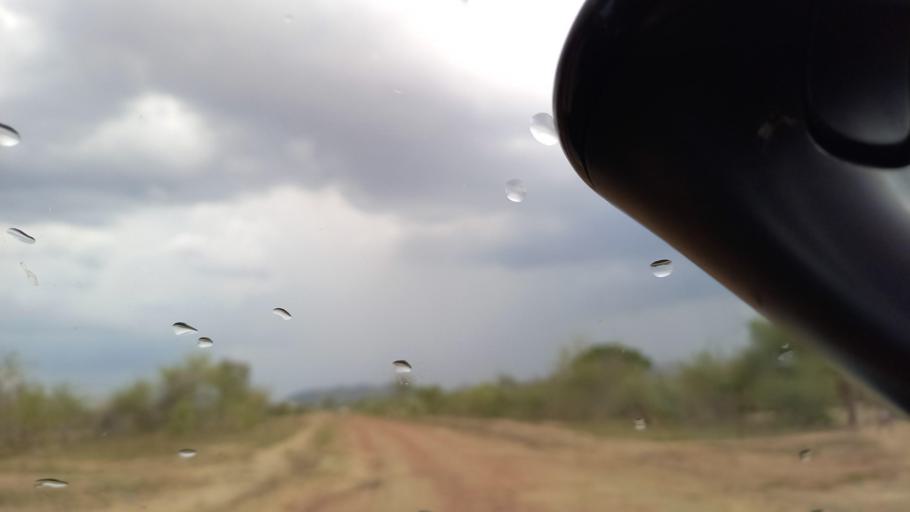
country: ZM
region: Lusaka
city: Kafue
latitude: -15.8536
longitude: 28.1131
